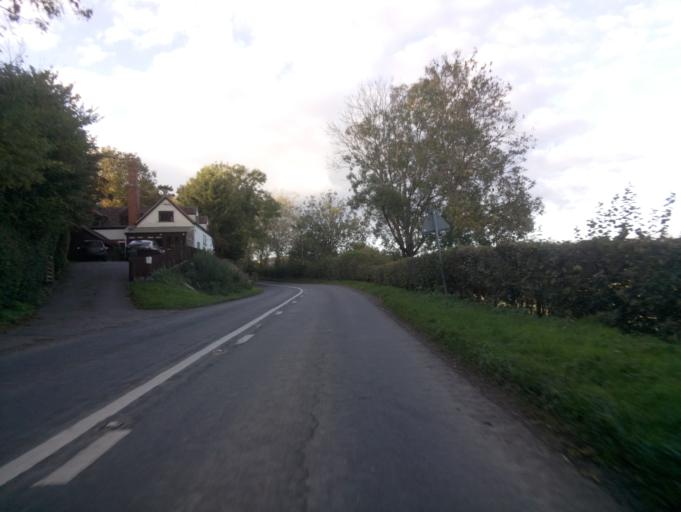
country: GB
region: England
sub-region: Herefordshire
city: Ledbury
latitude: 52.0409
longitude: -2.3976
